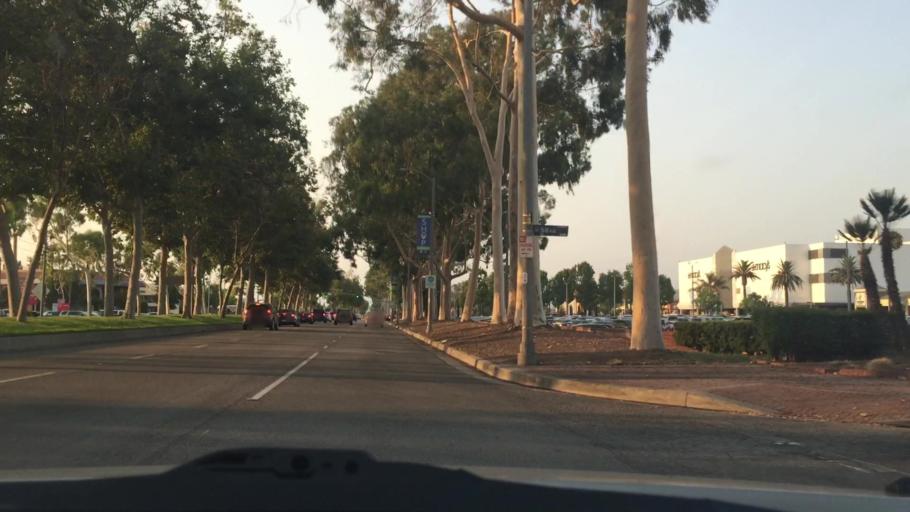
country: US
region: California
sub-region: Los Angeles County
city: Lakewood
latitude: 33.8481
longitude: -118.1424
